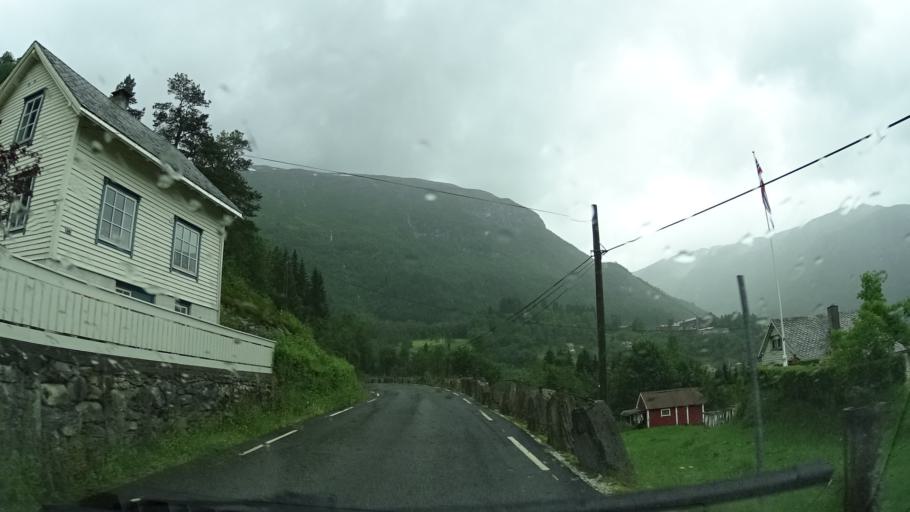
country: NO
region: Sogn og Fjordane
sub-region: Vik
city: Vik
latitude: 60.8293
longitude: 6.6821
